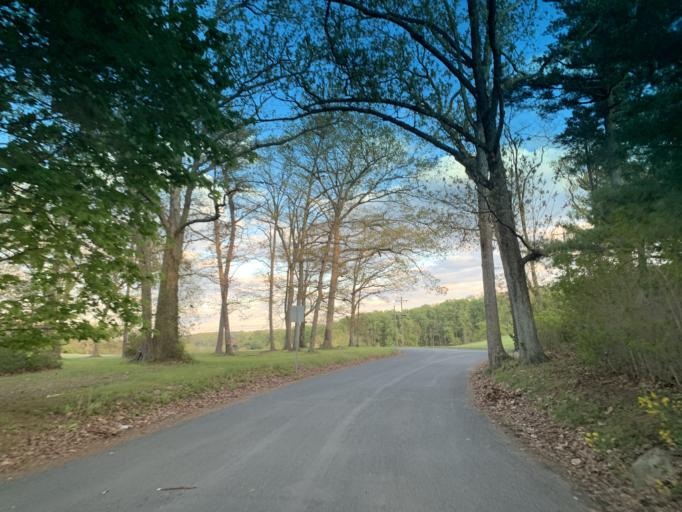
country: US
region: Maryland
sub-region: Harford County
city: Jarrettsville
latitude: 39.6235
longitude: -76.4259
